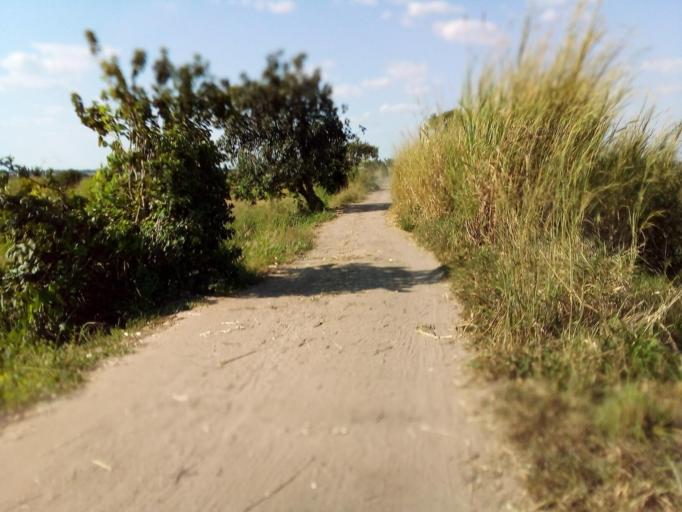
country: MZ
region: Zambezia
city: Quelimane
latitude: -17.5888
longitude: 36.8374
